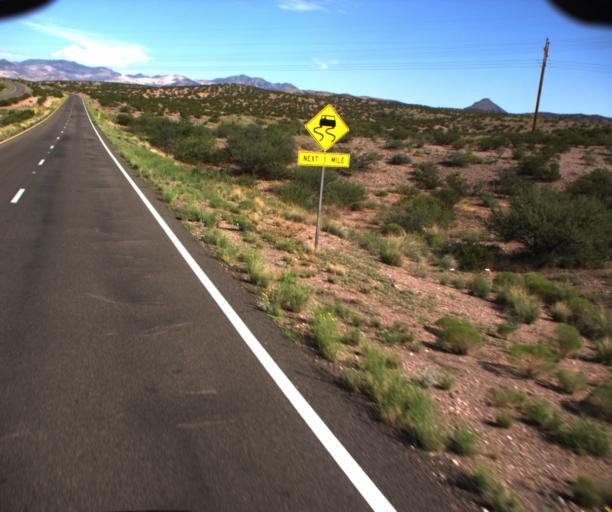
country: US
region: Arizona
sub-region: Greenlee County
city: Clifton
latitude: 32.9865
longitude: -109.2649
